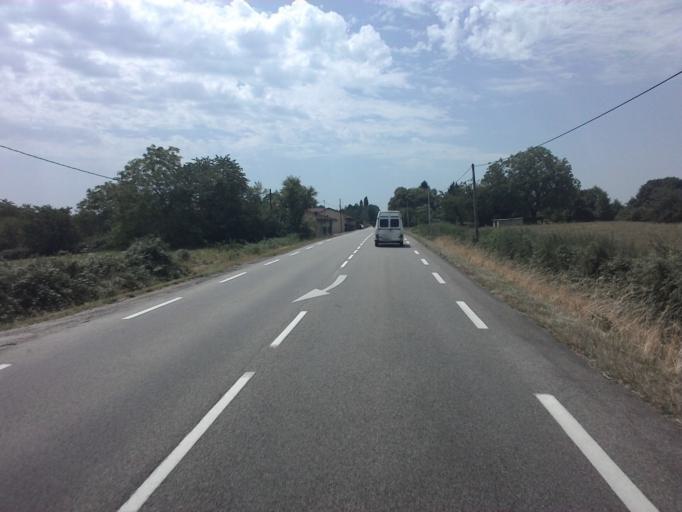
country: FR
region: Rhone-Alpes
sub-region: Departement de l'Ain
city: Saint-Etienne-du-Bois
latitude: 46.3002
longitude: 5.3013
